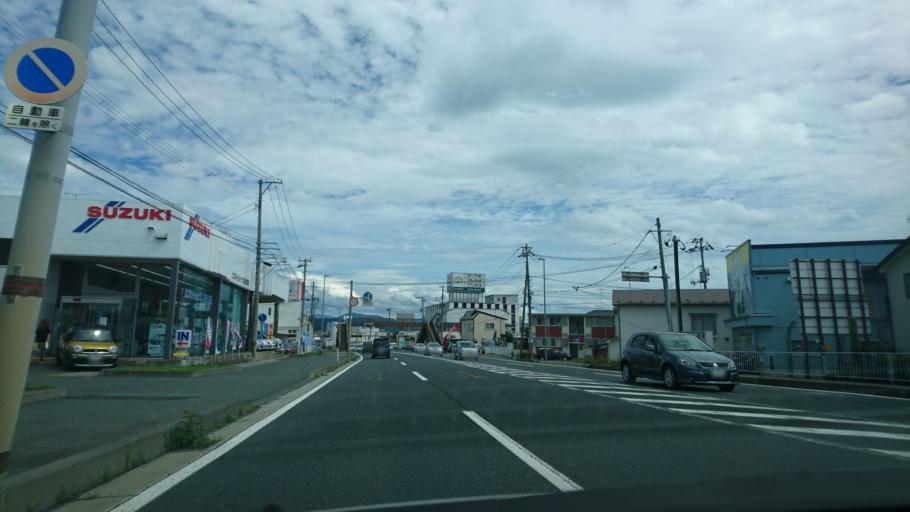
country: JP
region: Iwate
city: Morioka-shi
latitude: 39.7197
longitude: 141.1403
